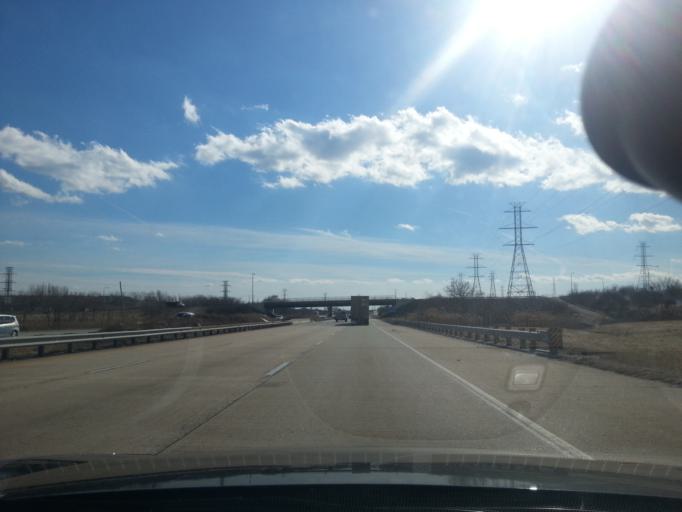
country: US
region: Delaware
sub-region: New Castle County
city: Edgemoor
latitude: 39.7377
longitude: -75.5200
